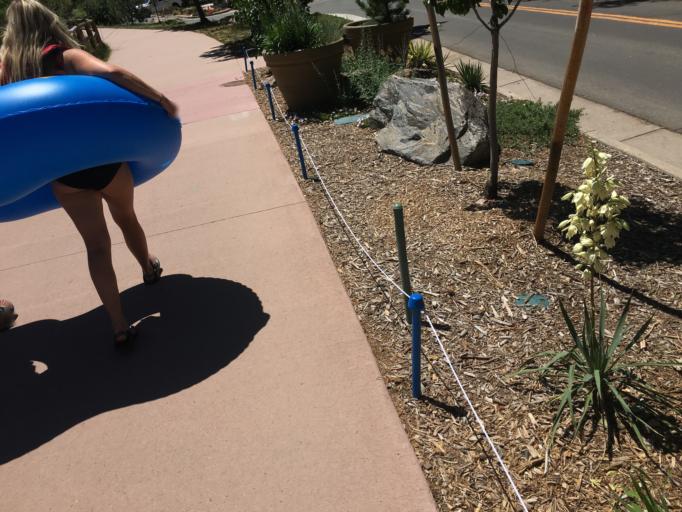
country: US
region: Colorado
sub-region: Jefferson County
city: Golden
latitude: 39.7542
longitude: -105.2299
